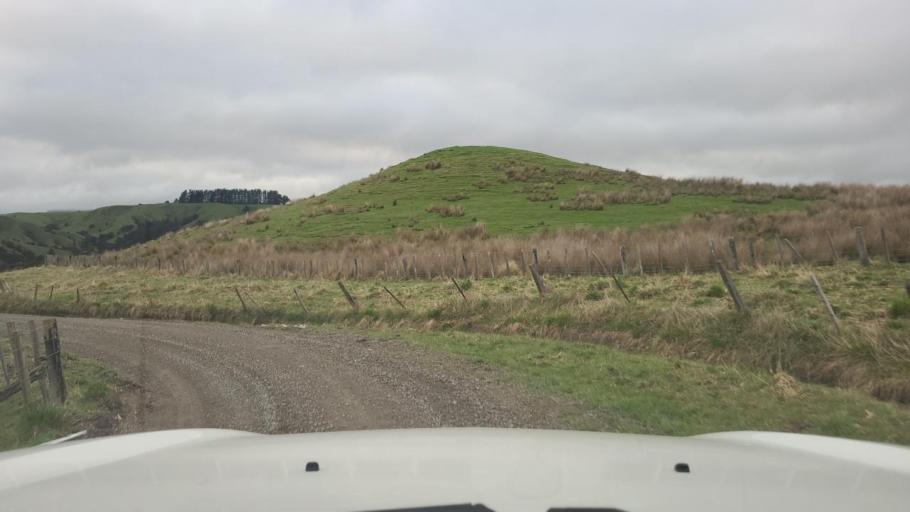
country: NZ
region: Wellington
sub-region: Masterton District
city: Masterton
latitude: -41.1659
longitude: 175.6925
